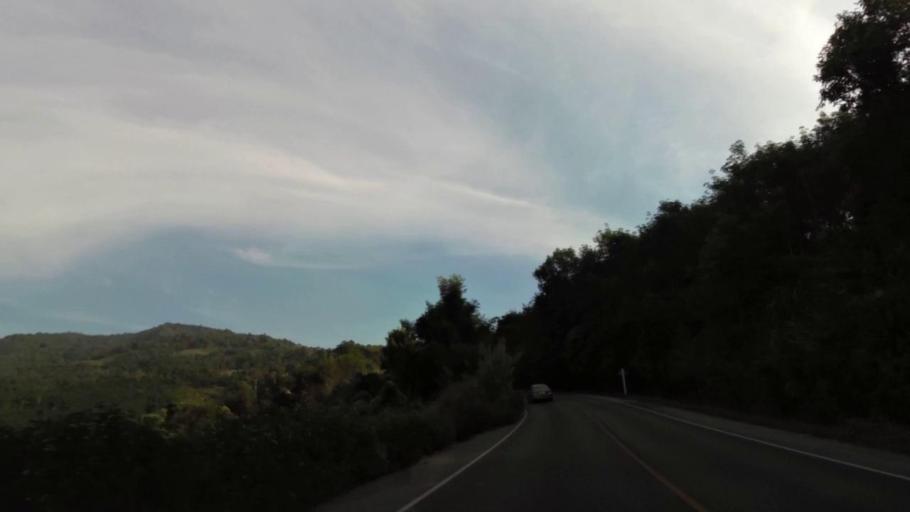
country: TH
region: Chiang Rai
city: Khun Tan
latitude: 19.8659
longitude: 100.4214
